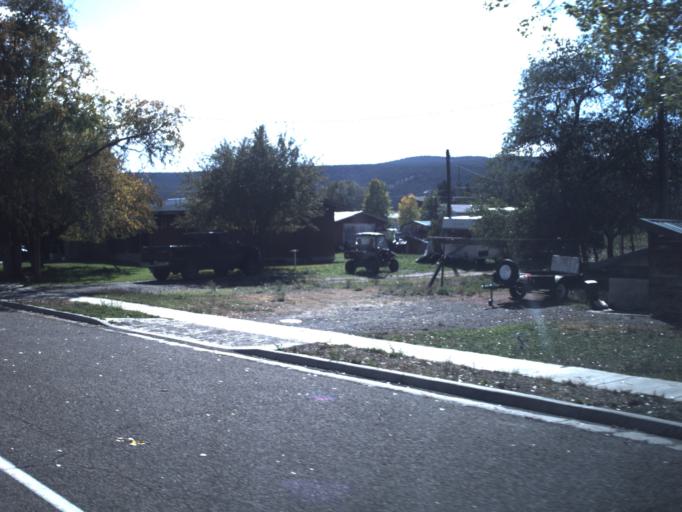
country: US
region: Utah
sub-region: Garfield County
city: Panguitch
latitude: 37.8161
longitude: -112.4356
